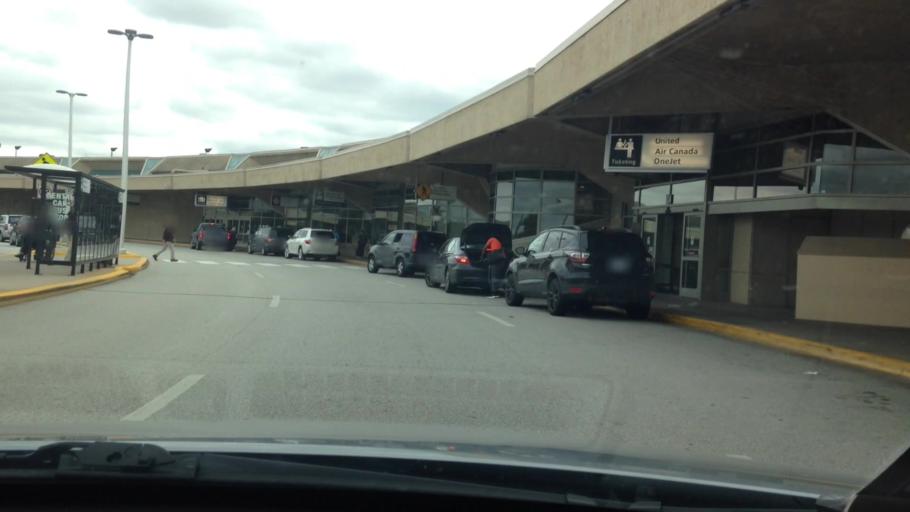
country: US
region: Missouri
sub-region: Platte County
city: Weatherby Lake
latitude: 39.2940
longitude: -94.7148
